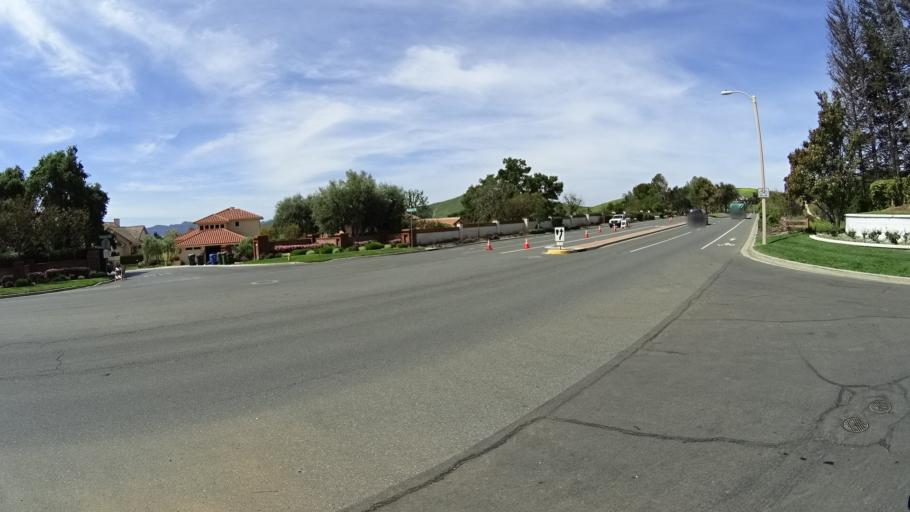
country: US
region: California
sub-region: Ventura County
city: Thousand Oaks
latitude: 34.1995
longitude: -118.8138
